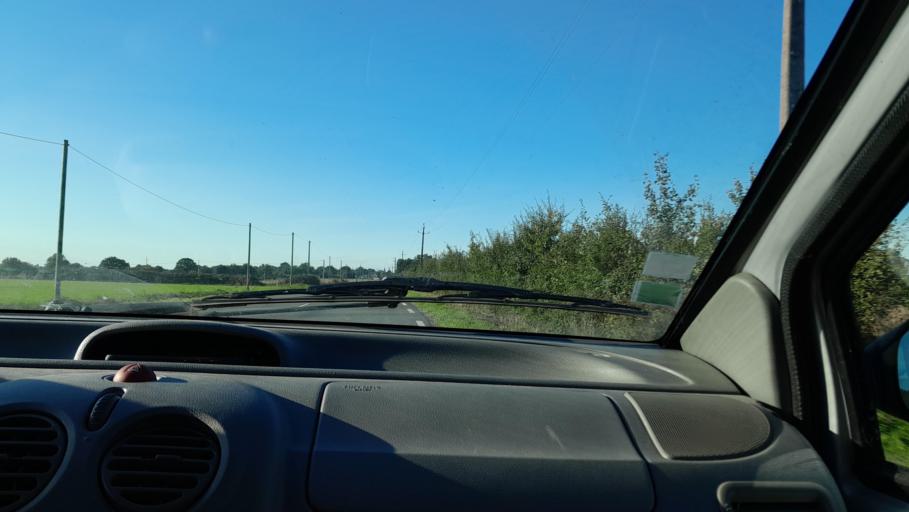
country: FR
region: Pays de la Loire
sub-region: Departement de la Mayenne
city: Ballots
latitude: 47.9281
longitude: -1.0710
